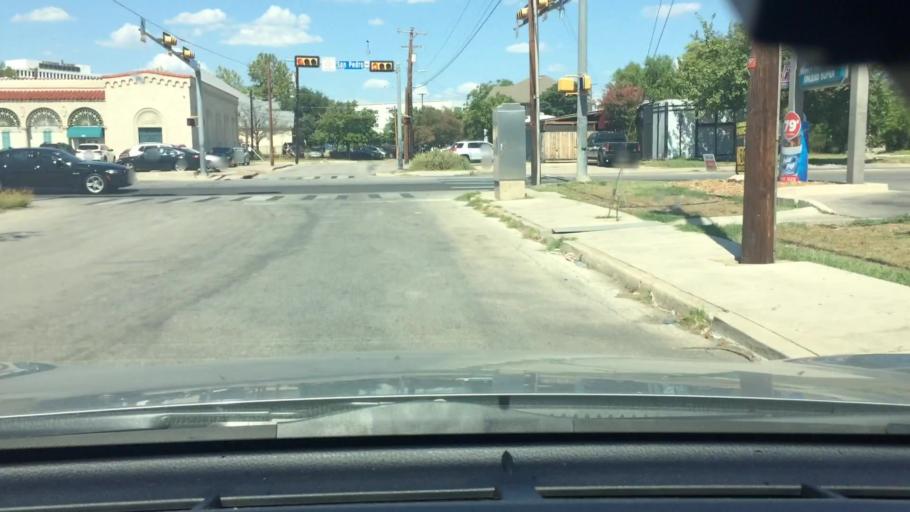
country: US
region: Texas
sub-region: Bexar County
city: San Antonio
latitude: 29.4366
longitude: -98.4970
